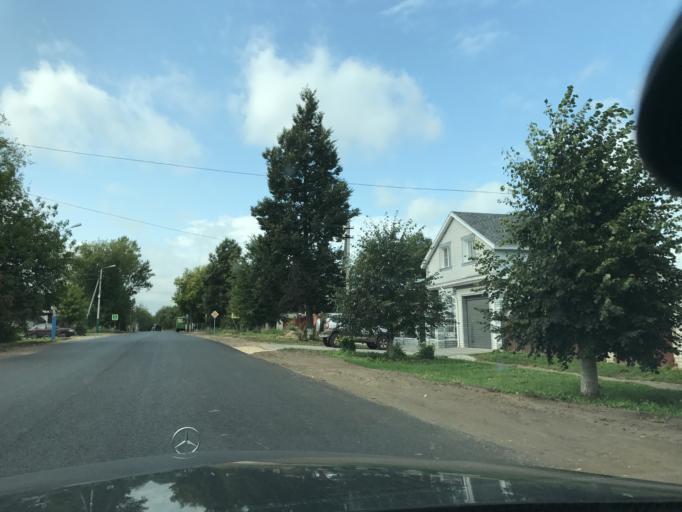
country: RU
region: Nizjnij Novgorod
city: Taremskoye
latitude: 55.9570
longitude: 43.0468
